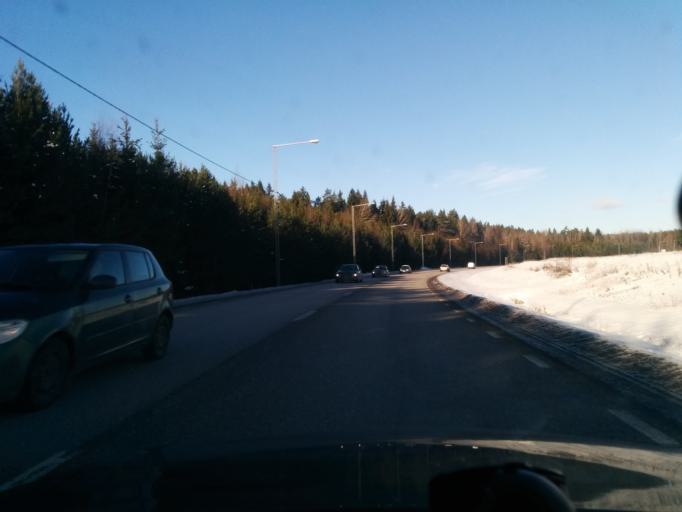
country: SE
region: Stockholm
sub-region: Taby Kommun
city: Taby
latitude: 59.4675
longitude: 18.1159
